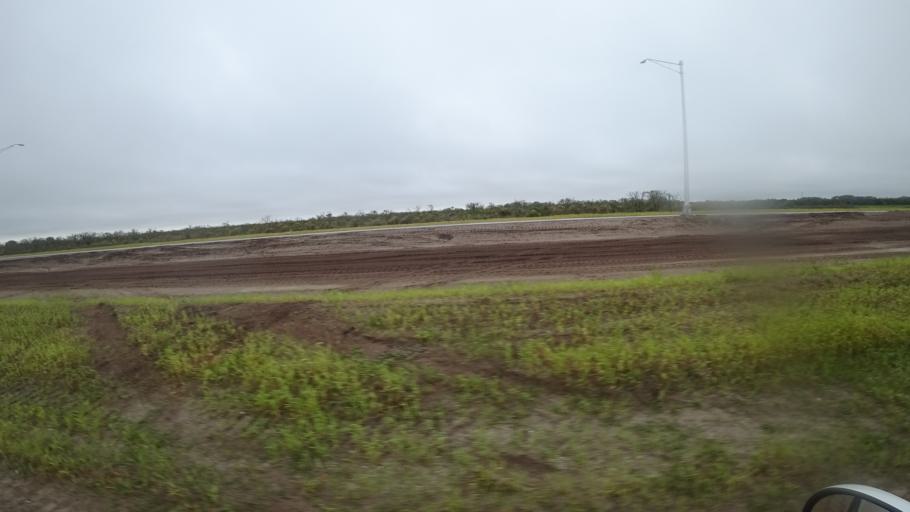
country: US
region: Florida
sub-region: Sarasota County
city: The Meadows
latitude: 27.4645
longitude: -82.3507
